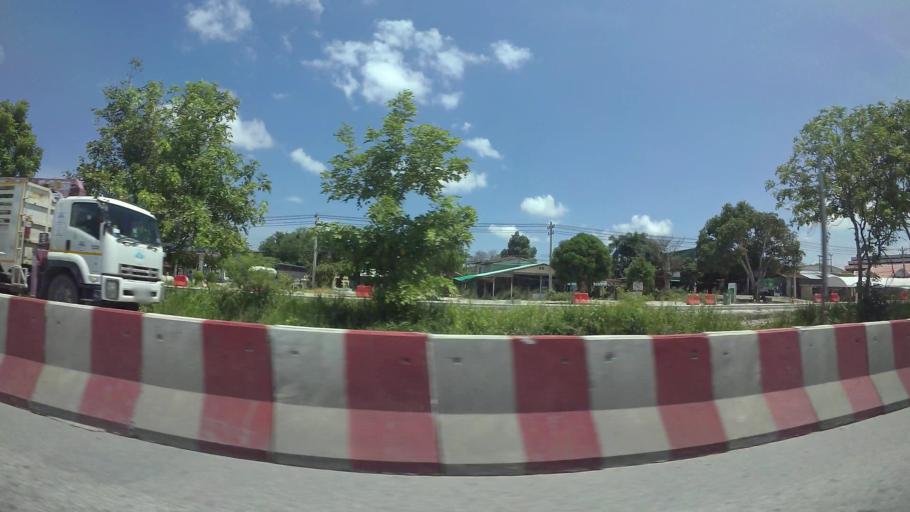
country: TH
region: Rayong
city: Rayong
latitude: 12.7230
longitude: 101.2198
